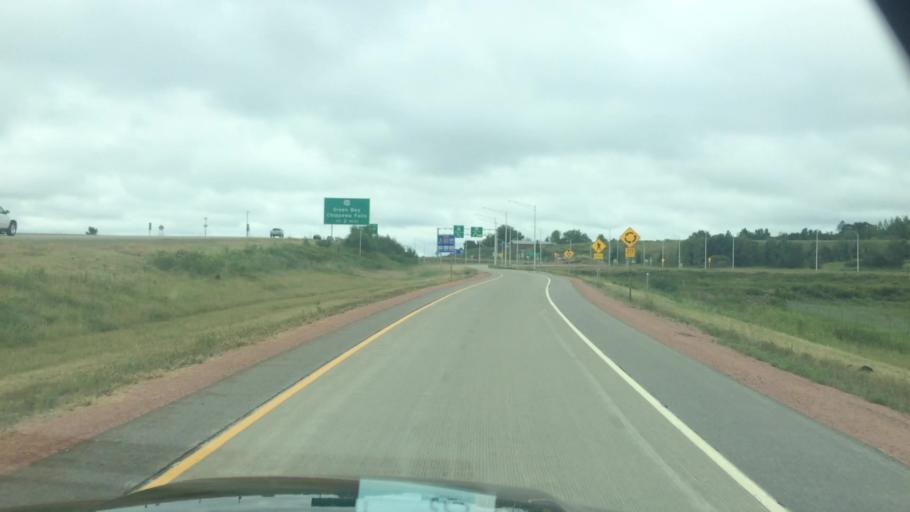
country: US
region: Wisconsin
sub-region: Marathon County
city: Wausau
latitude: 44.9937
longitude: -89.6577
